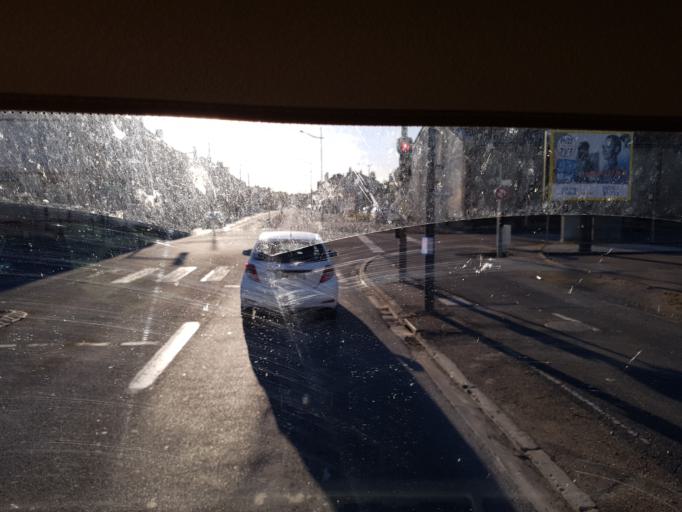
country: FR
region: Champagne-Ardenne
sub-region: Departement de l'Aube
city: Romilly-sur-Seine
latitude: 48.5108
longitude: 3.7251
